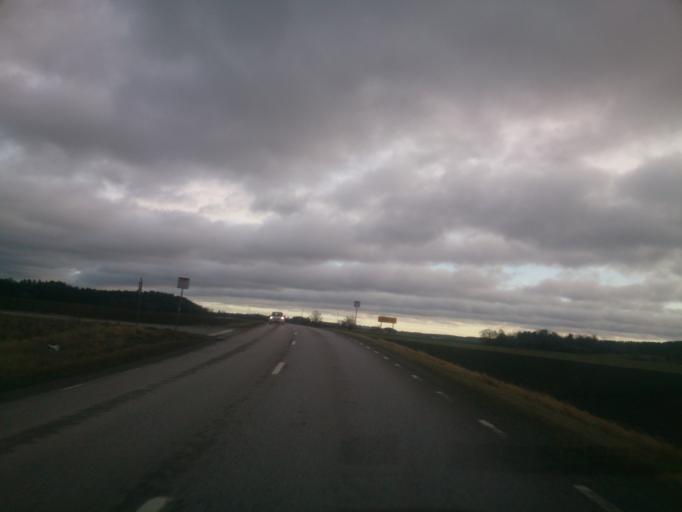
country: SE
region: OEstergoetland
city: Lindo
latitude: 58.5799
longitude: 16.3394
